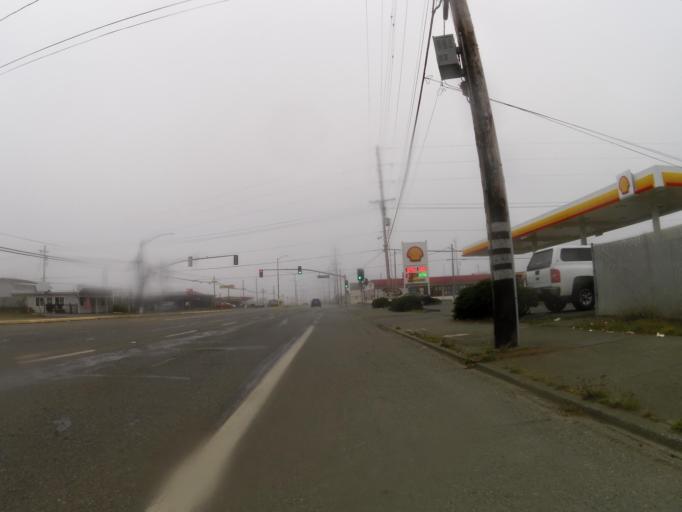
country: US
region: California
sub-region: Del Norte County
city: Crescent City
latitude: 41.7680
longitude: -124.1990
